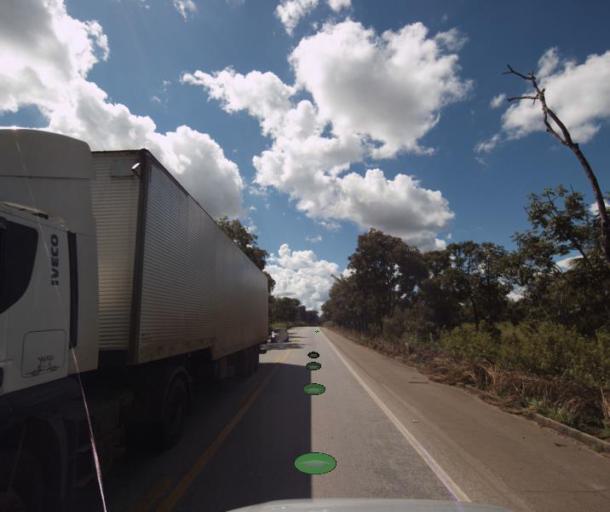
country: BR
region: Goias
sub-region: Porangatu
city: Porangatu
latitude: -13.6295
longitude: -49.0424
